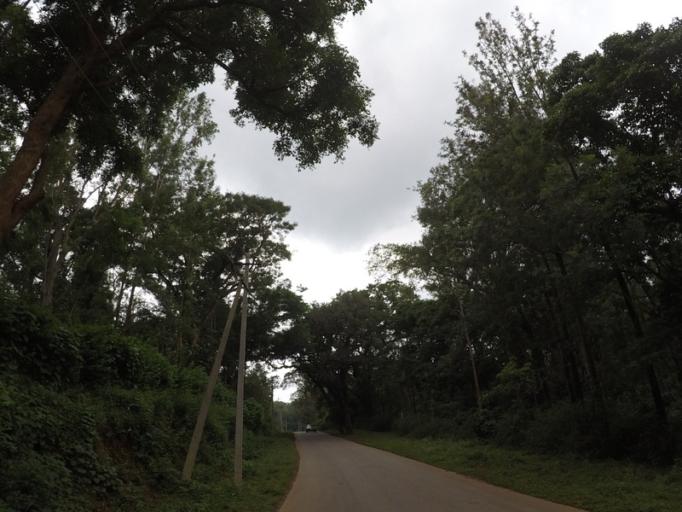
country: IN
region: Karnataka
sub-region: Chikmagalur
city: Chikmagalur
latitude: 13.4661
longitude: 75.7989
